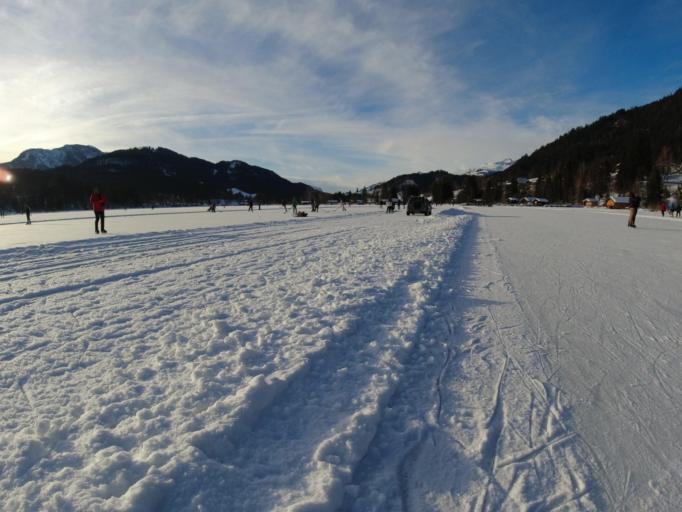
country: AT
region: Carinthia
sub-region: Politischer Bezirk Spittal an der Drau
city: Steinfeld
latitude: 46.7198
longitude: 13.2732
